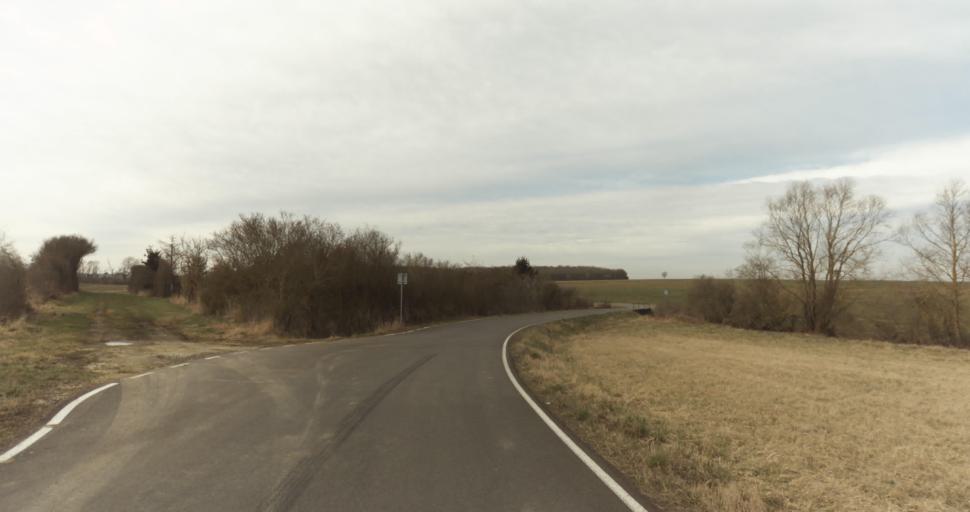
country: FR
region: Lorraine
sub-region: Departement de Meurthe-et-Moselle
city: Jarny
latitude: 49.1365
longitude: 5.8589
